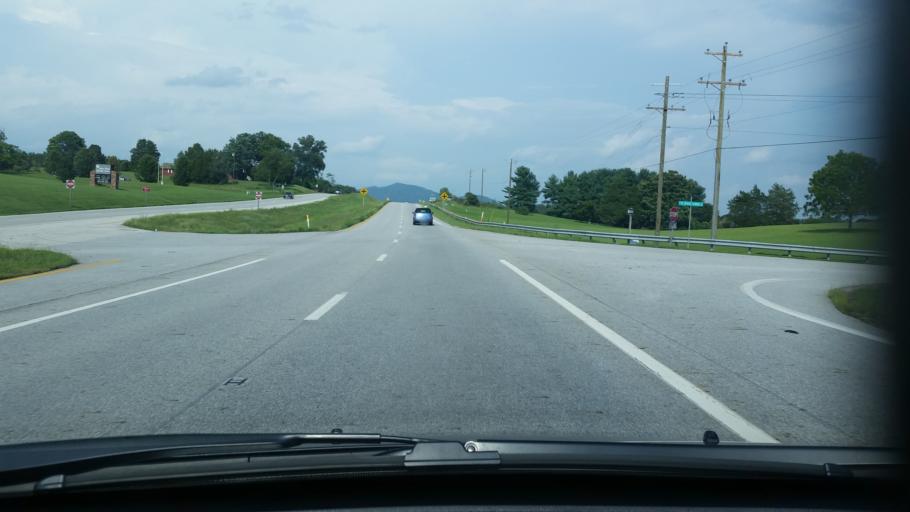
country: US
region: Virginia
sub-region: Nelson County
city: Lovingston
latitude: 37.7135
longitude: -78.9150
